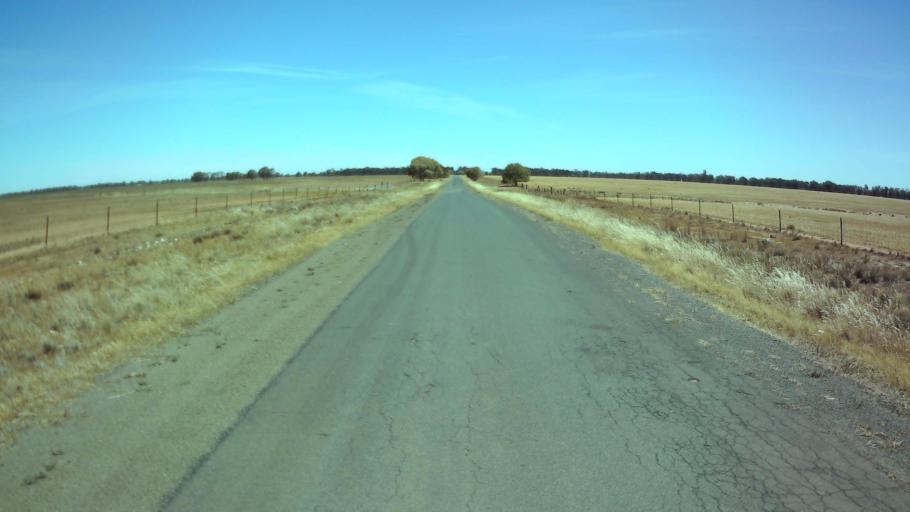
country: AU
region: New South Wales
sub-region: Weddin
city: Grenfell
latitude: -33.8513
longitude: 147.6955
